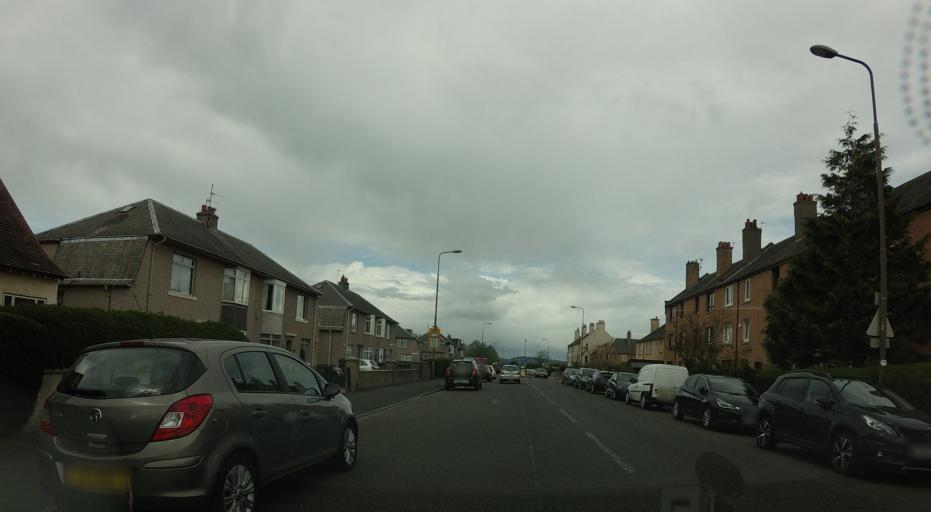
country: GB
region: Scotland
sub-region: Edinburgh
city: Edinburgh
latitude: 55.9755
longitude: -3.2389
